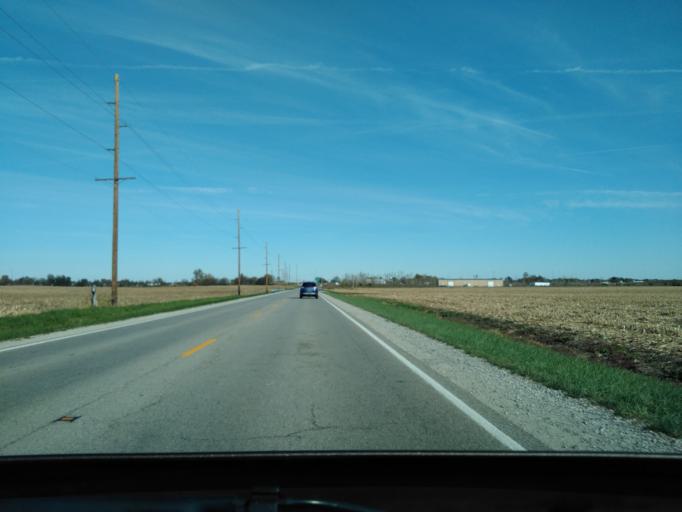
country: US
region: Illinois
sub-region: Madison County
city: Saint Jacob
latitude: 38.7535
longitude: -89.8005
